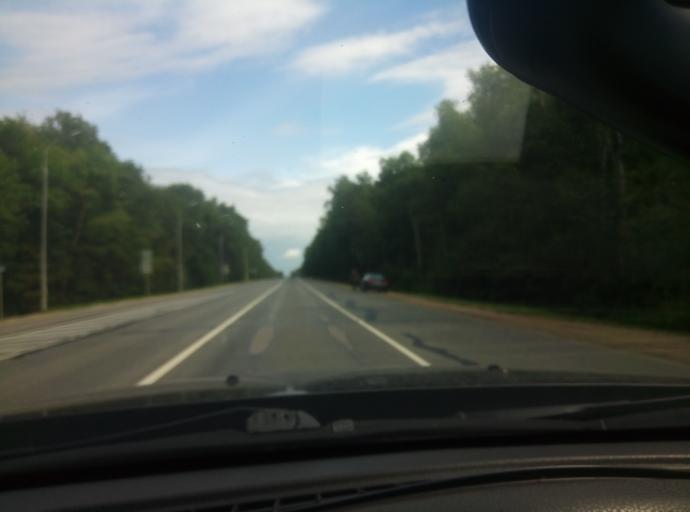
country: RU
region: Tula
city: Barsuki
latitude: 54.2675
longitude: 37.5337
